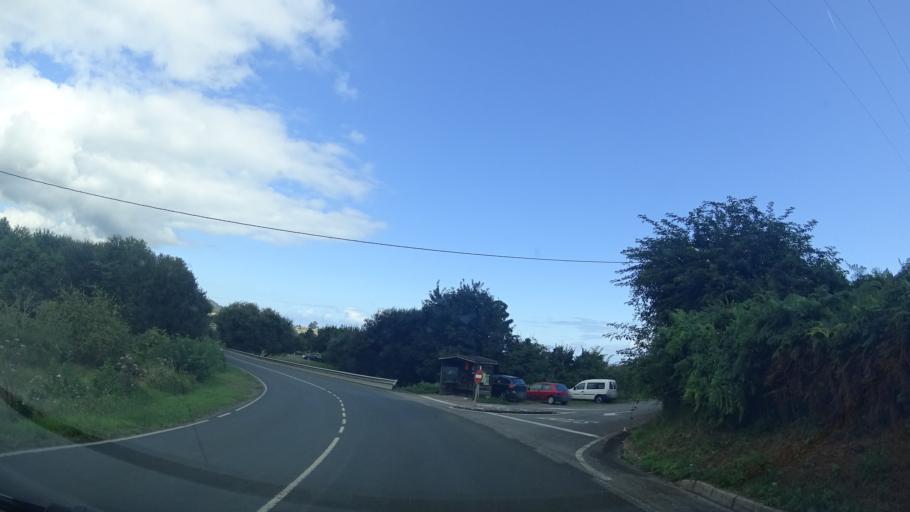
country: ES
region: Asturias
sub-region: Province of Asturias
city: Colunga
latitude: 43.4715
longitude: -5.2131
